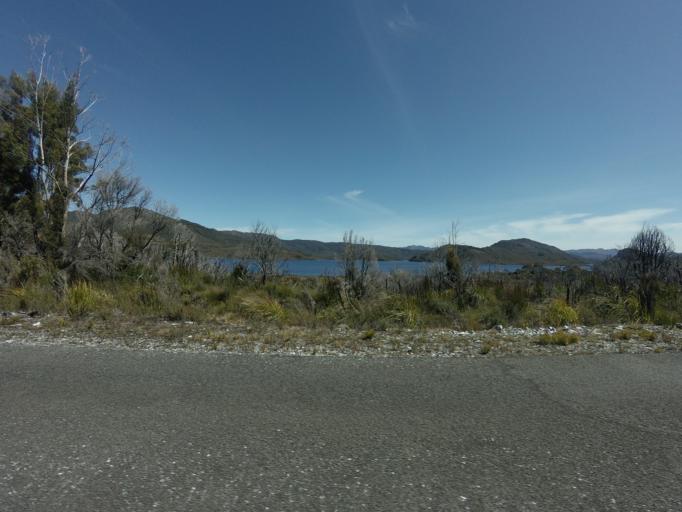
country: AU
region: Tasmania
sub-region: Huon Valley
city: Geeveston
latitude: -42.8441
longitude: 146.1655
